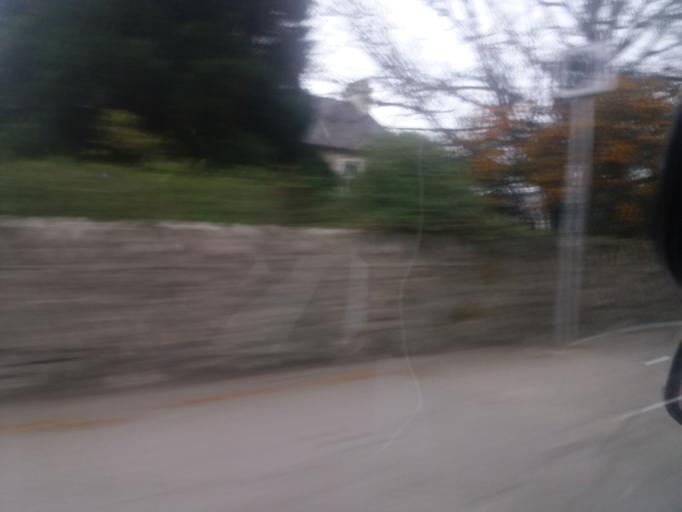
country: IE
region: Munster
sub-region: County Limerick
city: Adare
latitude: 52.5617
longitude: -8.7937
